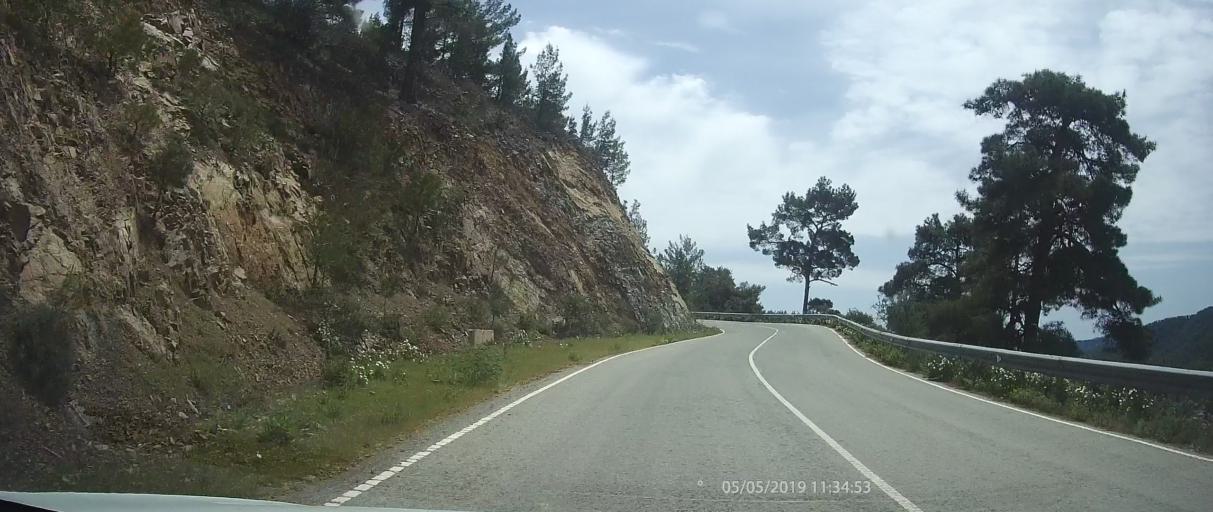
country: CY
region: Lefkosia
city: Kato Pyrgos
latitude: 34.9659
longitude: 32.6501
